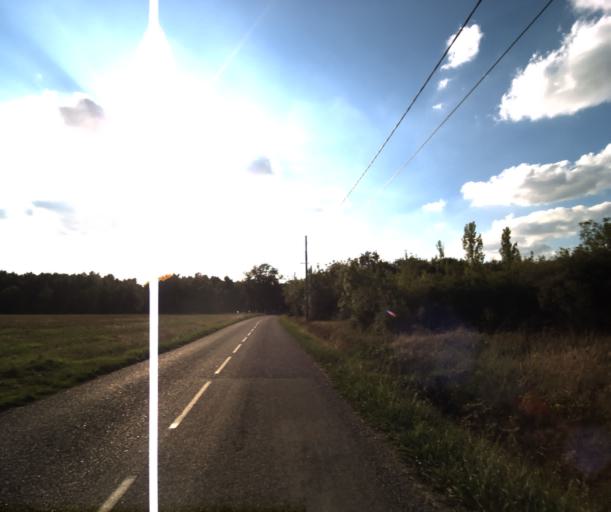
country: FR
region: Midi-Pyrenees
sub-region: Departement de la Haute-Garonne
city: Labastidette
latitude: 43.4787
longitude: 1.2521
